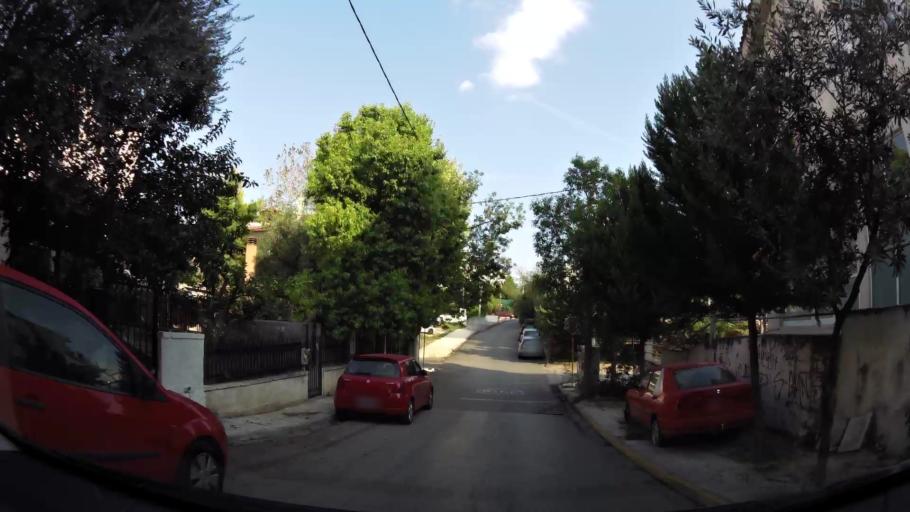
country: GR
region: Attica
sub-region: Nomarchia Athinas
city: Irakleio
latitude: 38.0484
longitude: 23.7804
